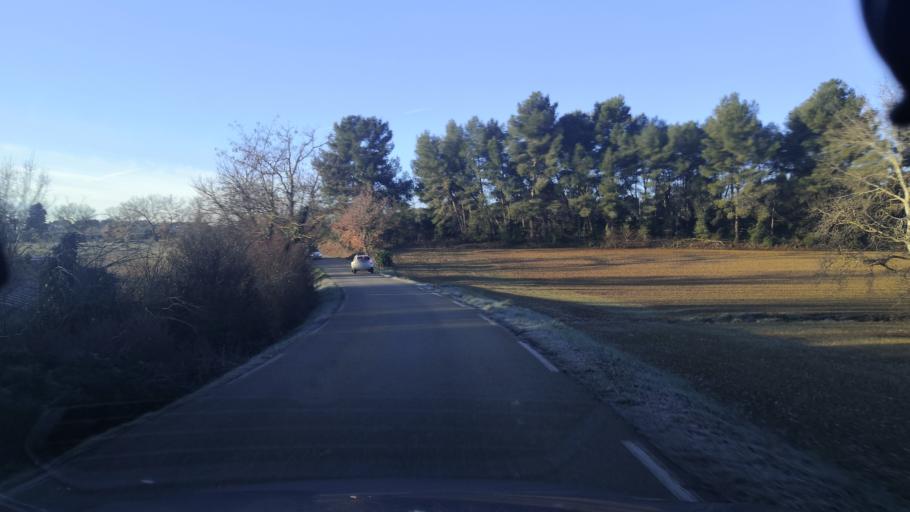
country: FR
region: Provence-Alpes-Cote d'Azur
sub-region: Departement des Bouches-du-Rhone
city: Aix-en-Provence
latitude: 43.5188
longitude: 5.4066
